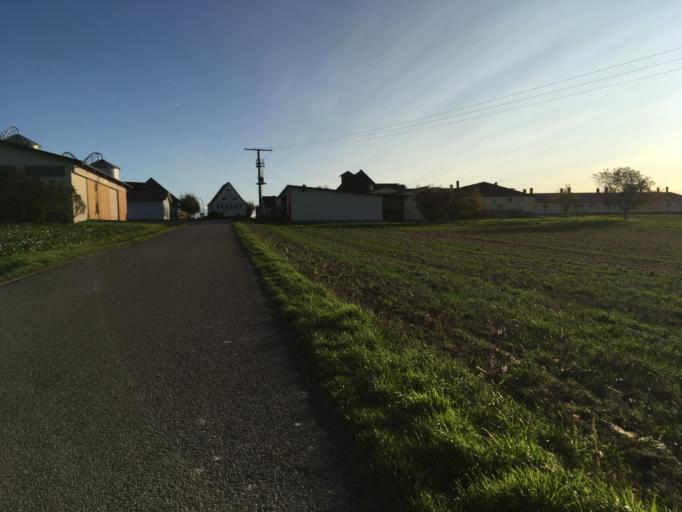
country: DE
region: Baden-Wuerttemberg
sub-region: Regierungsbezirk Stuttgart
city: Neuenstein
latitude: 49.2301
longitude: 9.6111
